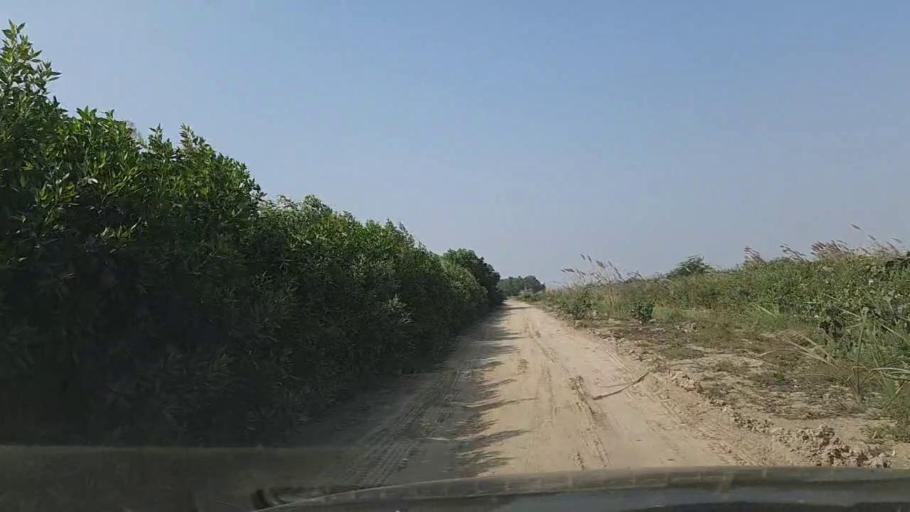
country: PK
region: Sindh
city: Gharo
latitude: 24.7220
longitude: 67.6786
